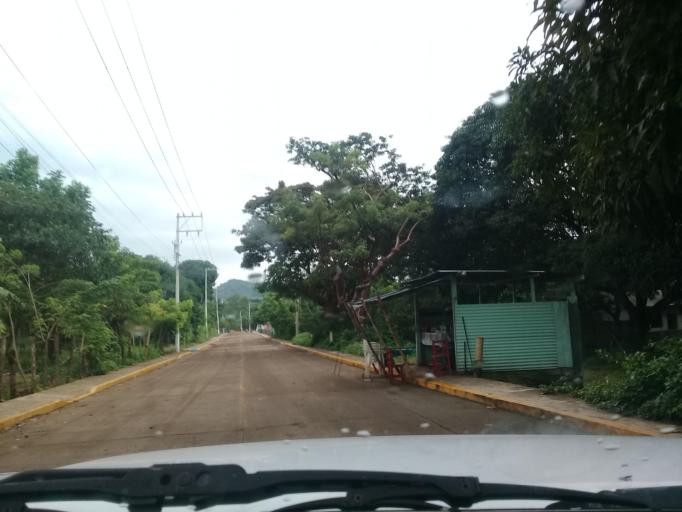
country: MX
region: Veracruz
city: San Andres Tuxtla
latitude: 18.4354
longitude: -95.2106
